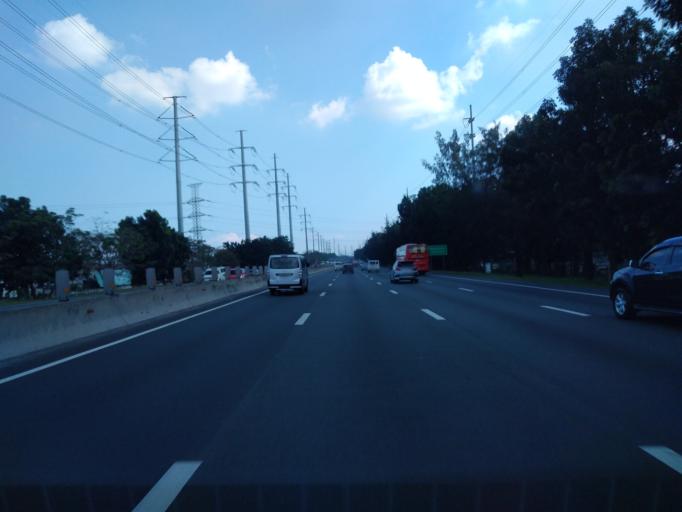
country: PH
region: Calabarzon
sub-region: Province of Cavite
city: Carmona
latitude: 14.3090
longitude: 121.0733
